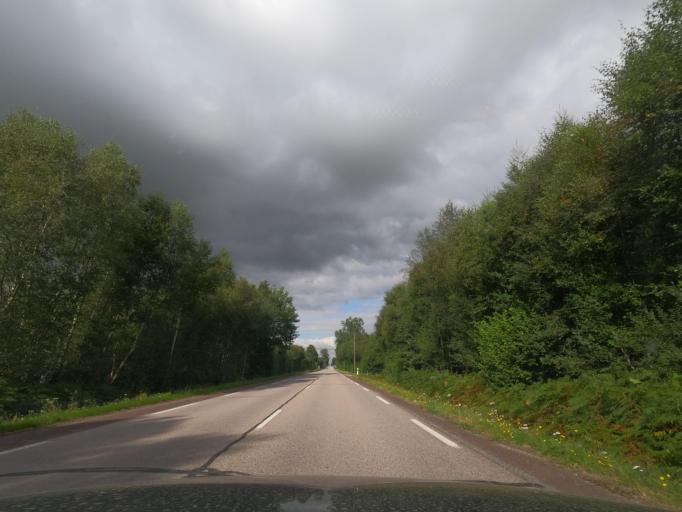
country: FR
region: Lower Normandy
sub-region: Departement de l'Orne
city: Gace
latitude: 48.8472
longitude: 0.3528
